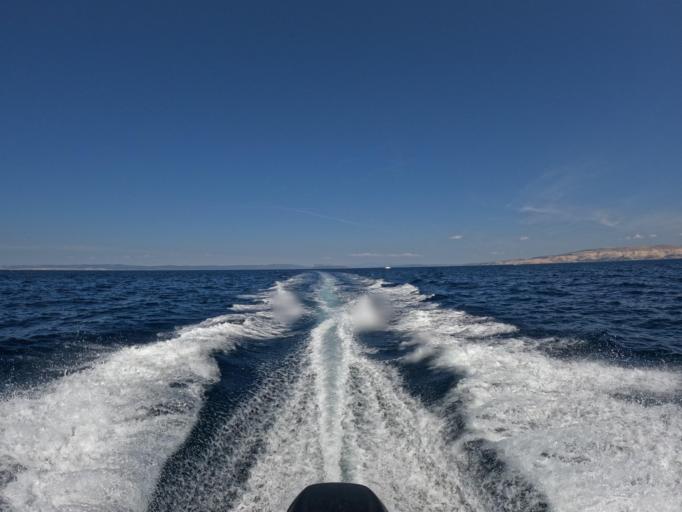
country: HR
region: Primorsko-Goranska
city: Lopar
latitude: 44.8696
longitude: 14.6726
